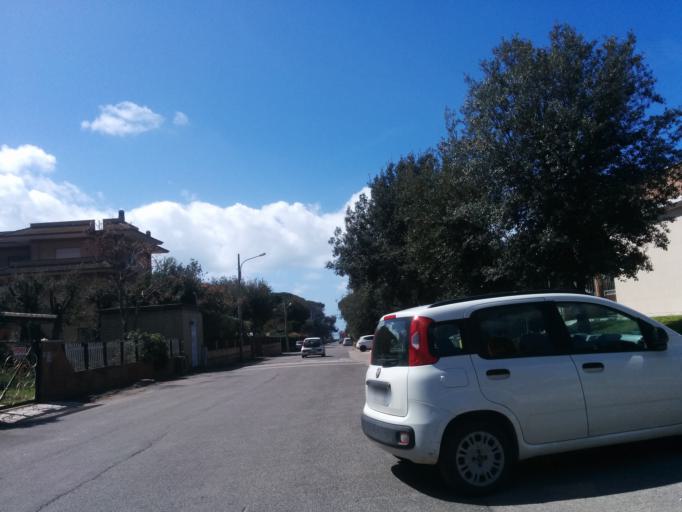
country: IT
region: Latium
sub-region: Citta metropolitana di Roma Capitale
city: Lavinio
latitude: 41.4967
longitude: 12.5909
